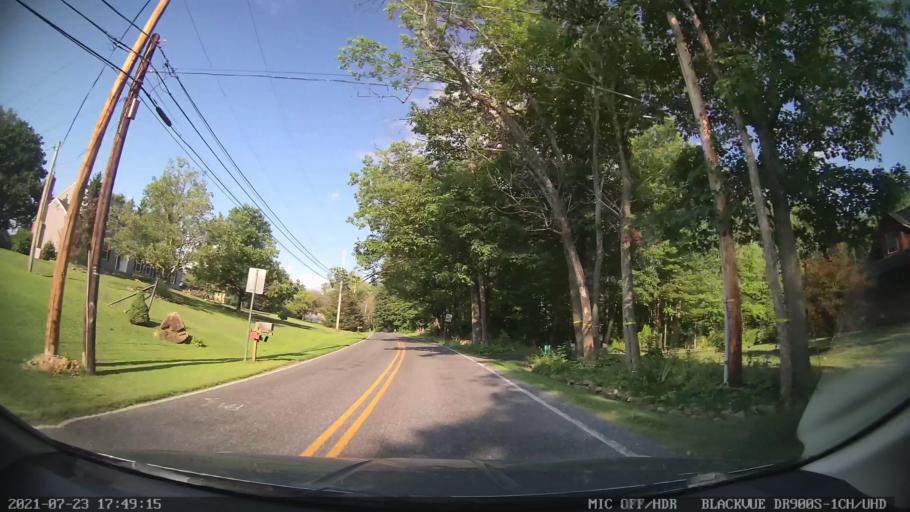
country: US
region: Pennsylvania
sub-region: Berks County
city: Red Lion
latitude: 40.4918
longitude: -75.6102
